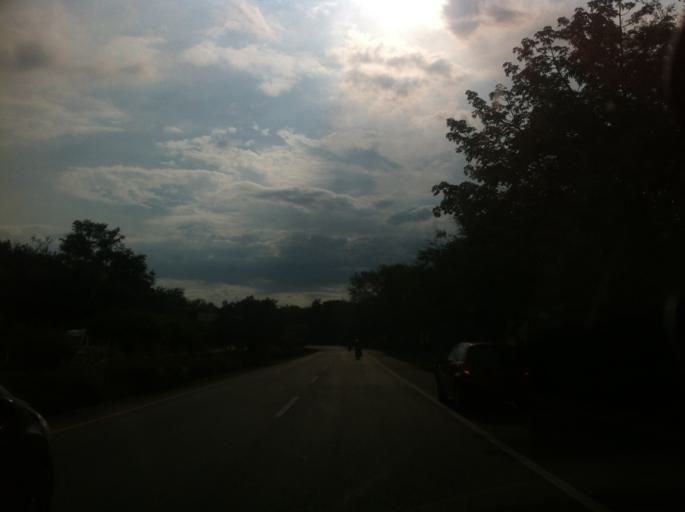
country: CO
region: Valle del Cauca
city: San Pedro
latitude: 3.9717
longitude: -76.2543
